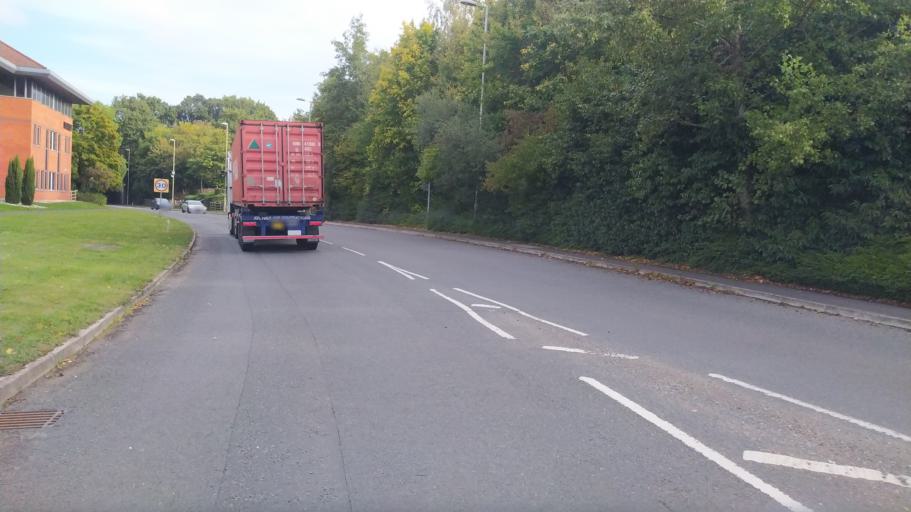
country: GB
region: England
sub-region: Hampshire
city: Hook
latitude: 51.2793
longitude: -0.9521
